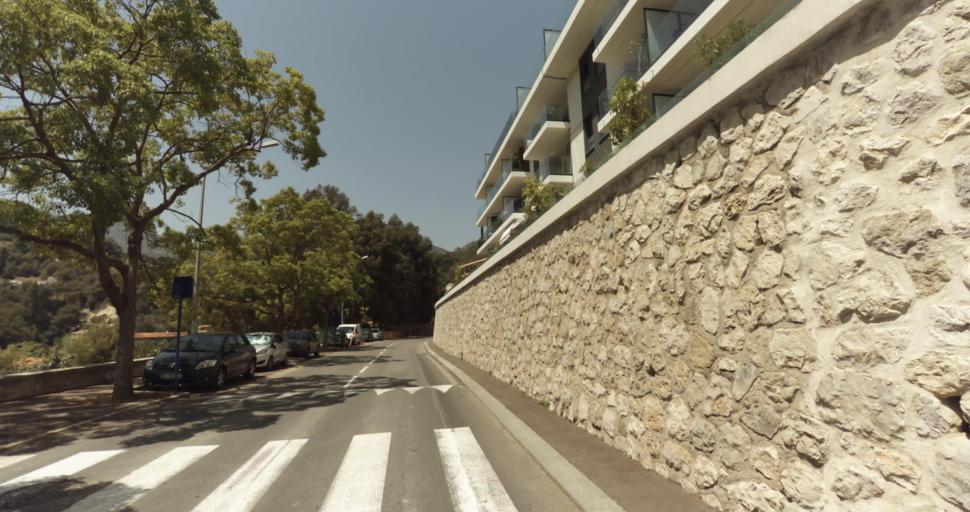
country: FR
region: Provence-Alpes-Cote d'Azur
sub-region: Departement des Alpes-Maritimes
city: Roquebrune-Cap-Martin
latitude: 43.7714
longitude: 7.4788
